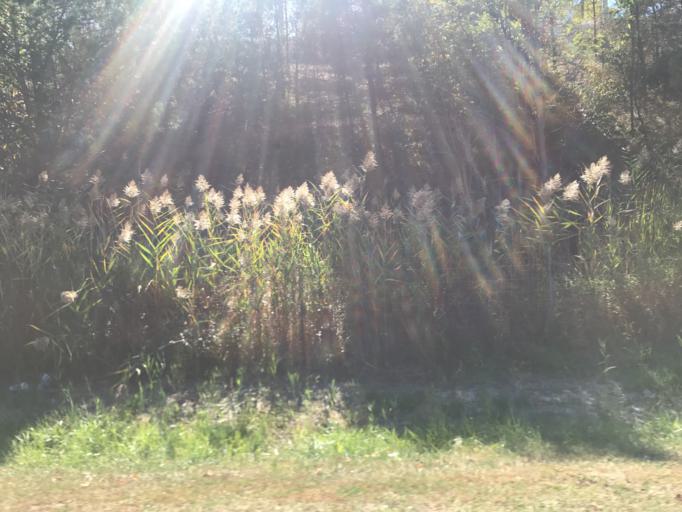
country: US
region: Ohio
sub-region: Cuyahoga County
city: North Royalton
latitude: 41.3080
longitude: -81.7477
